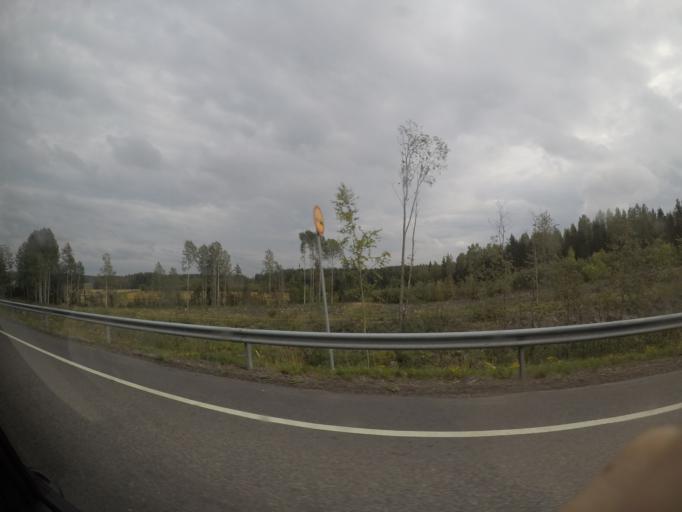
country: FI
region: Haeme
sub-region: Haemeenlinna
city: Parola
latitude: 61.0900
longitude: 24.4014
